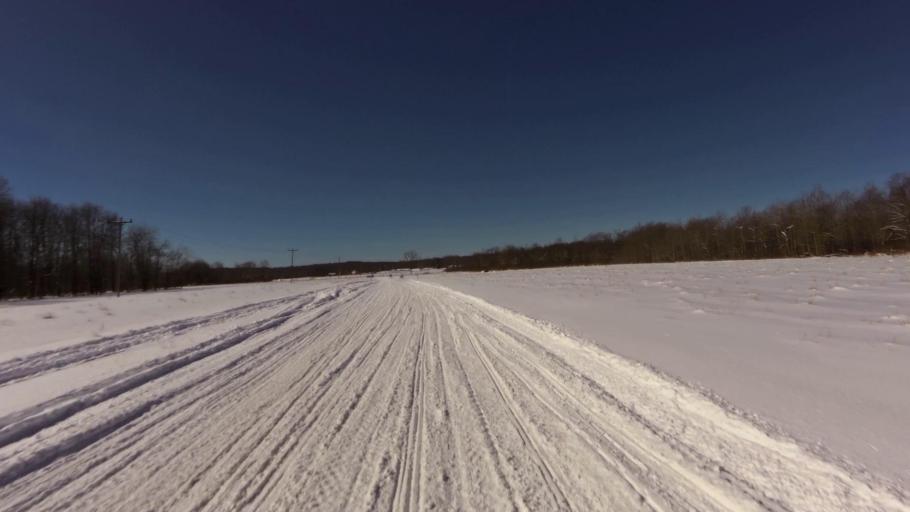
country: US
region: New York
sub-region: Chautauqua County
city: Mayville
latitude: 42.2729
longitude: -79.4771
